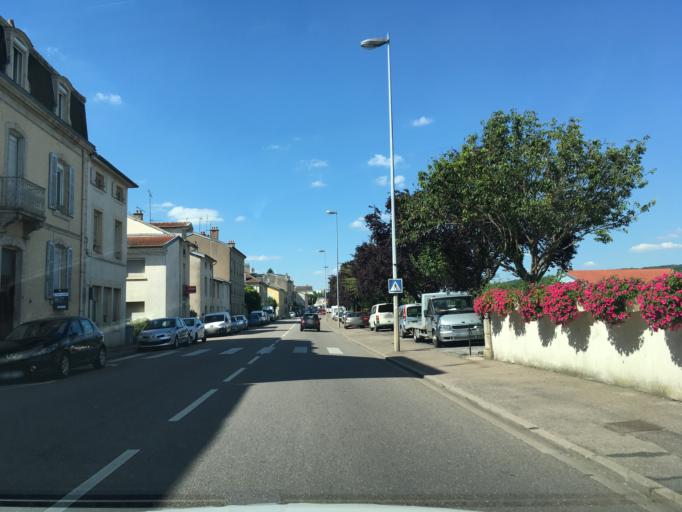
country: FR
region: Lorraine
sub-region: Departement de Meurthe-et-Moselle
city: Maxeville
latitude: 48.7096
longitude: 6.1672
